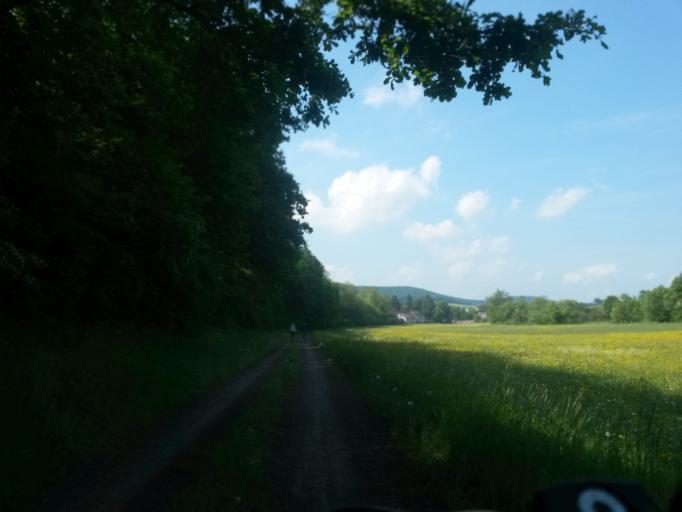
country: DE
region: Bavaria
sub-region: Regierungsbezirk Unterfranken
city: Euerdorf
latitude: 50.1541
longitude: 10.0337
